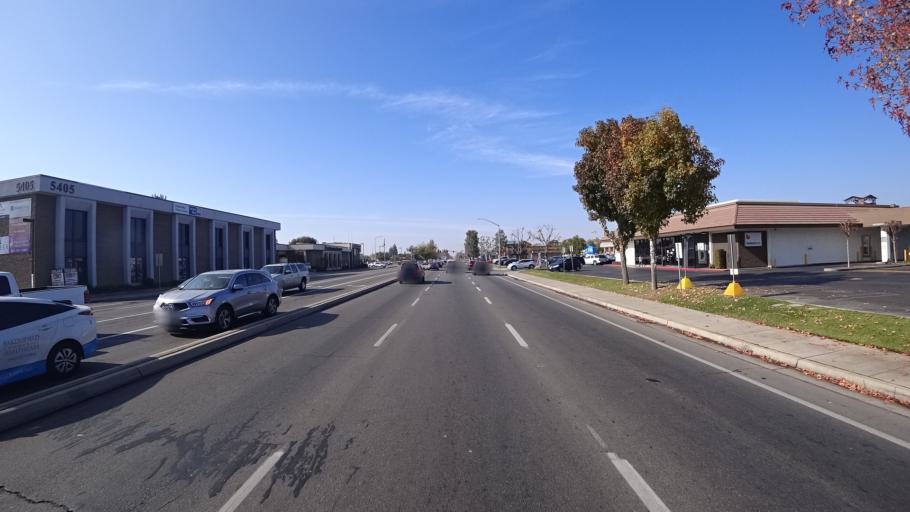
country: US
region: California
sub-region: Kern County
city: Bakersfield
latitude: 35.3544
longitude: -119.0617
